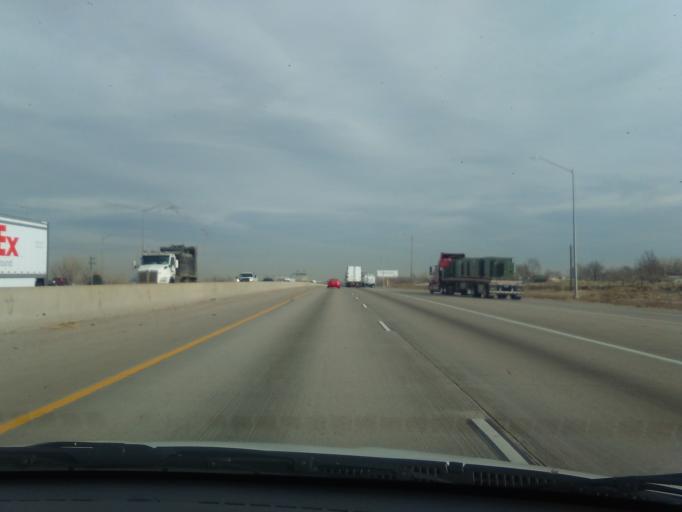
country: US
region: Colorado
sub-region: Adams County
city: Derby
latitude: 39.8484
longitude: -104.9219
